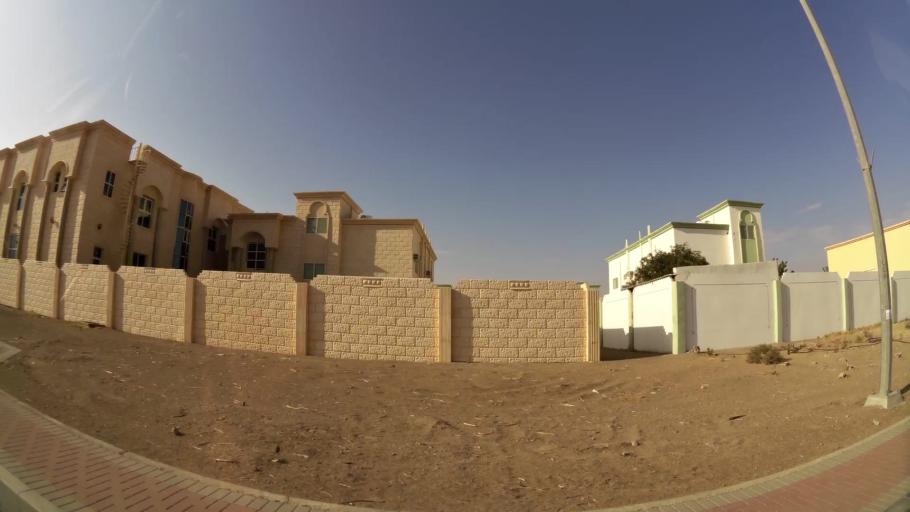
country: AE
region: Abu Dhabi
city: Al Ain
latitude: 24.0550
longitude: 55.8428
